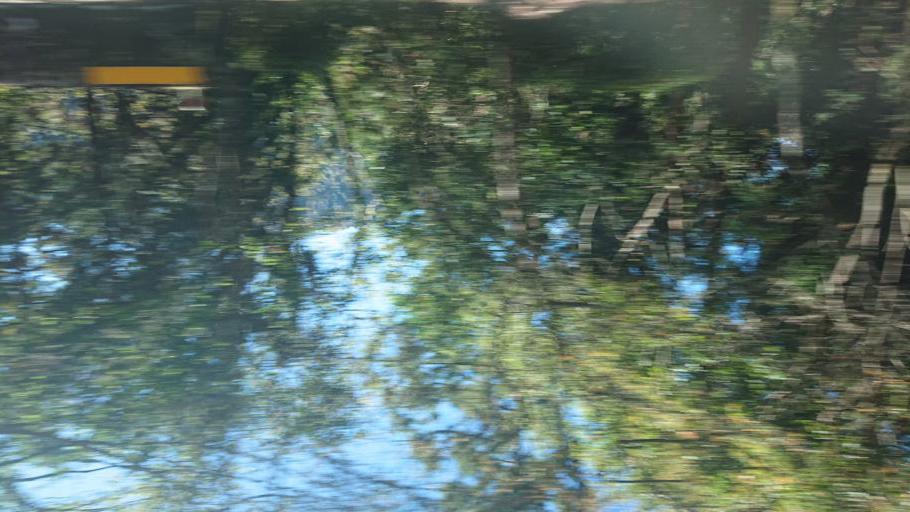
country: TW
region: Taiwan
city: Lugu
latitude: 23.4770
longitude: 120.8379
